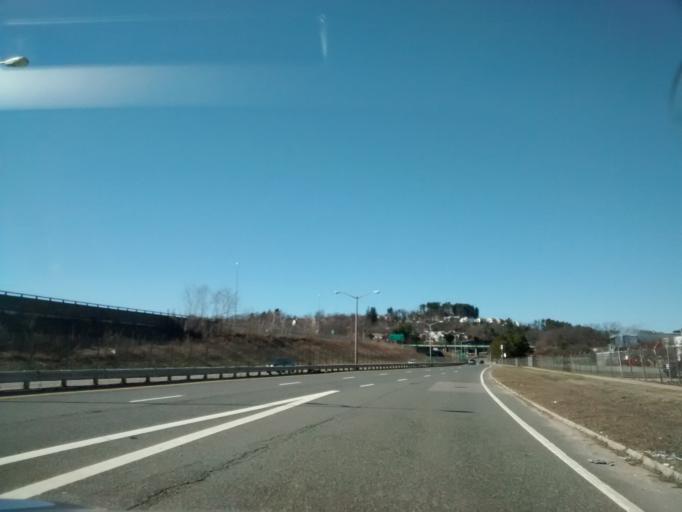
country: US
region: Massachusetts
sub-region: Worcester County
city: Worcester
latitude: 42.3012
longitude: -71.8052
